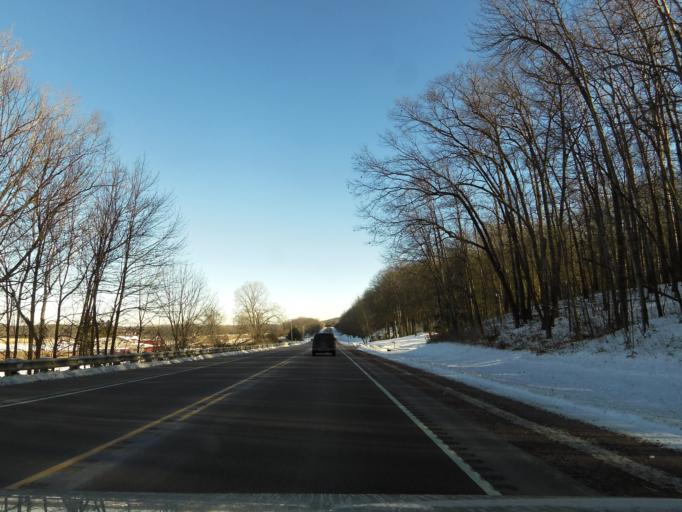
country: US
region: Wisconsin
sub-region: Columbia County
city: Portage
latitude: 43.5089
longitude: -89.5608
